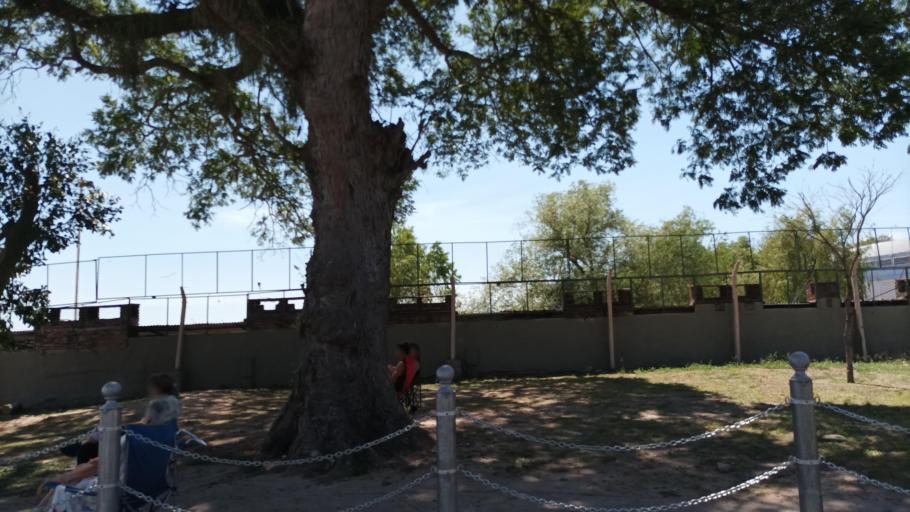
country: AR
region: Corrientes
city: Corrientes
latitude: -27.4588
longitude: -58.8309
